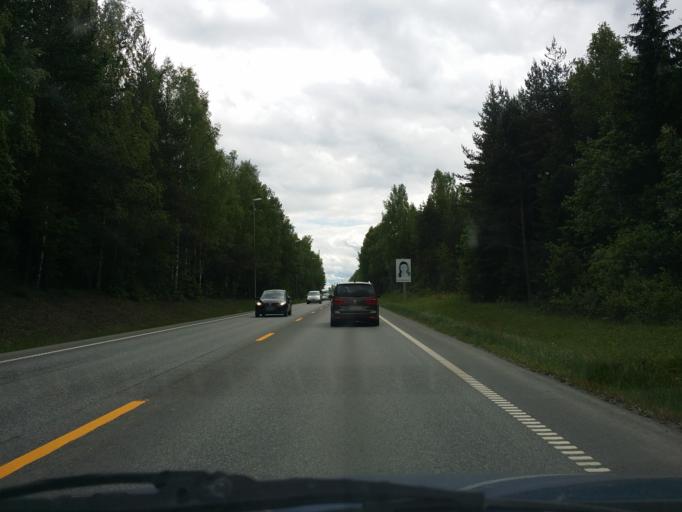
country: NO
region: Hedmark
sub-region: Stange
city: Stange
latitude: 60.7534
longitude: 11.1954
